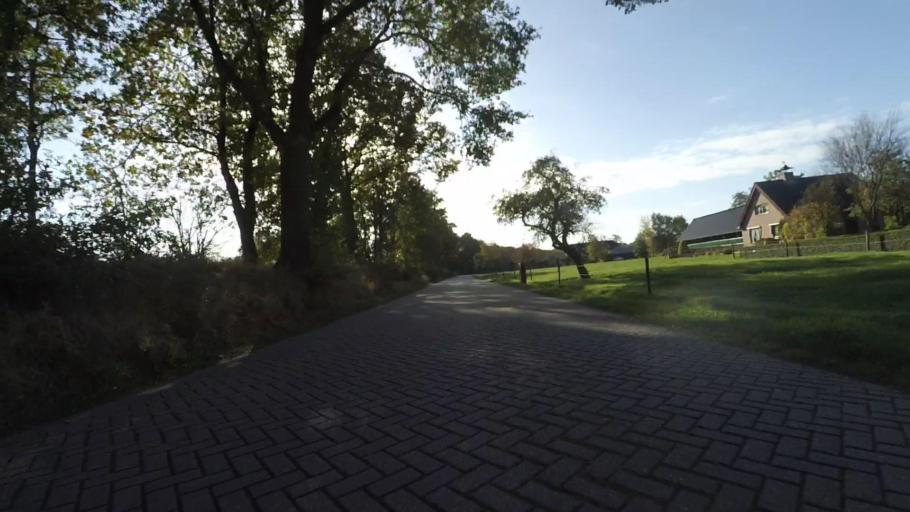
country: NL
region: Gelderland
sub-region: Gemeente Nijkerk
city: Nijkerk
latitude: 52.2527
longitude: 5.5370
